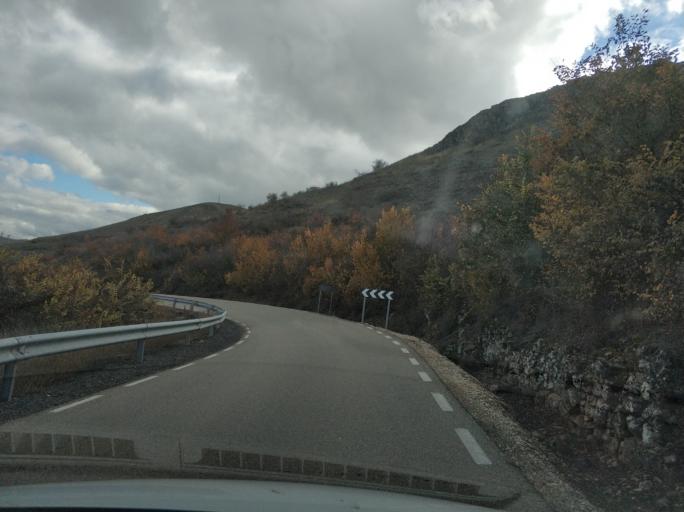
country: ES
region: Castille and Leon
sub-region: Provincia de Soria
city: Medinaceli
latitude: 41.1642
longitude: -2.4324
